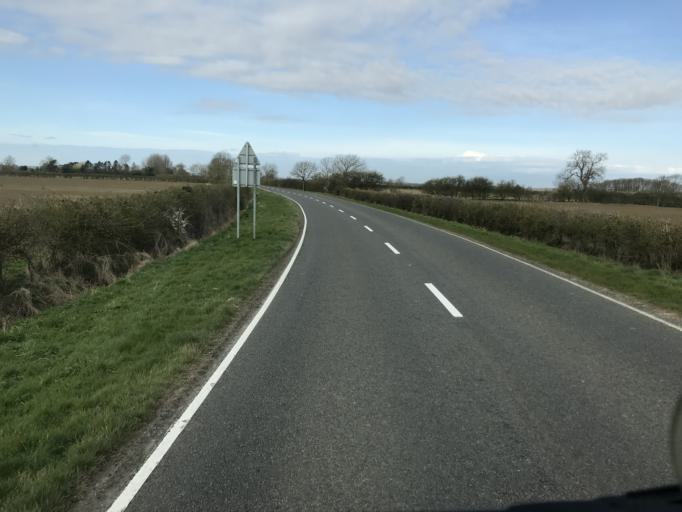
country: GB
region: England
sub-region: Lincolnshire
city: Market Rasen
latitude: 53.3957
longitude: -0.4090
